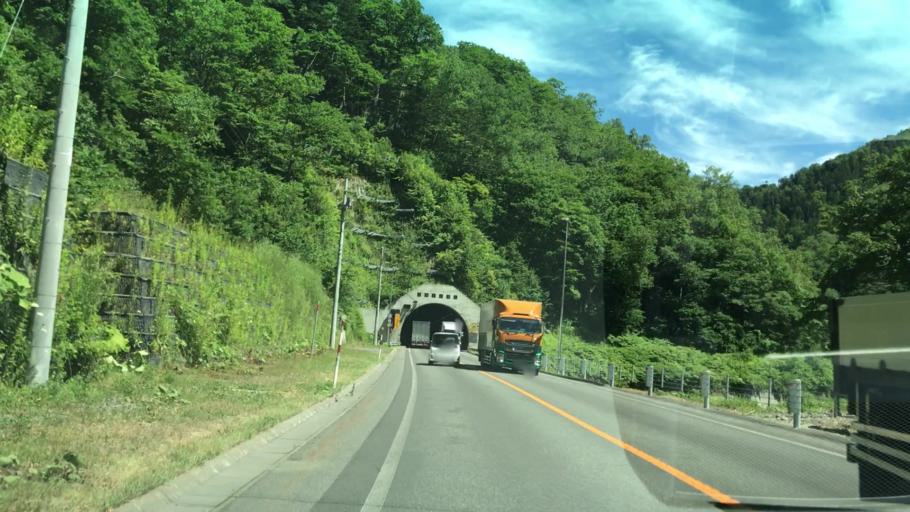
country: JP
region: Hokkaido
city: Shimo-furano
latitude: 42.9557
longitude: 142.6117
